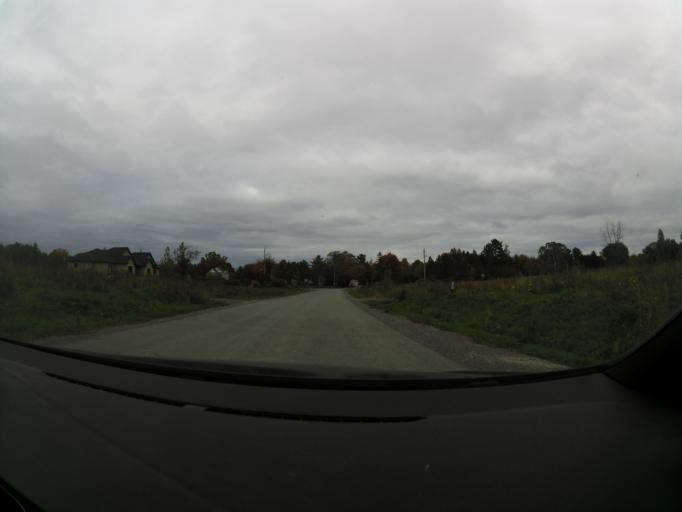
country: CA
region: Ontario
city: Bells Corners
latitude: 45.3815
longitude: -75.9699
